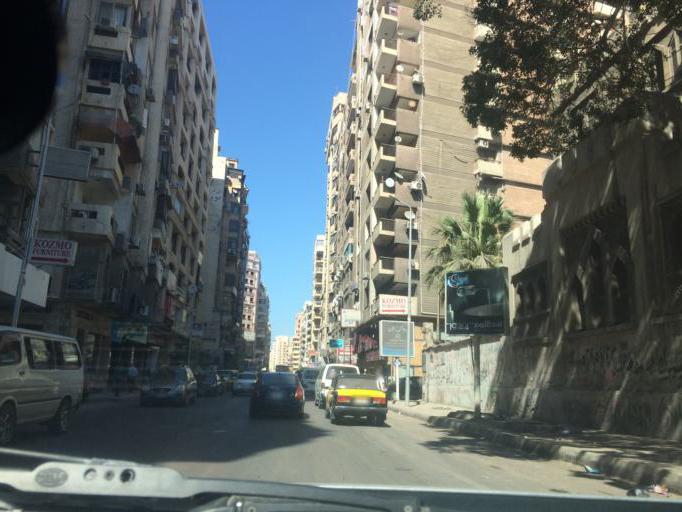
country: EG
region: Alexandria
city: Alexandria
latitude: 31.2455
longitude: 29.9738
